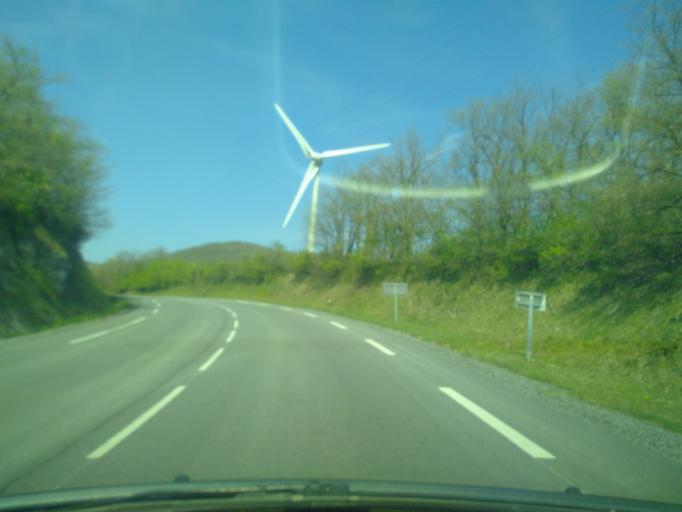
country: FR
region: Rhone-Alpes
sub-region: Departement de la Drome
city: Crest
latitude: 44.6402
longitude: 4.9861
